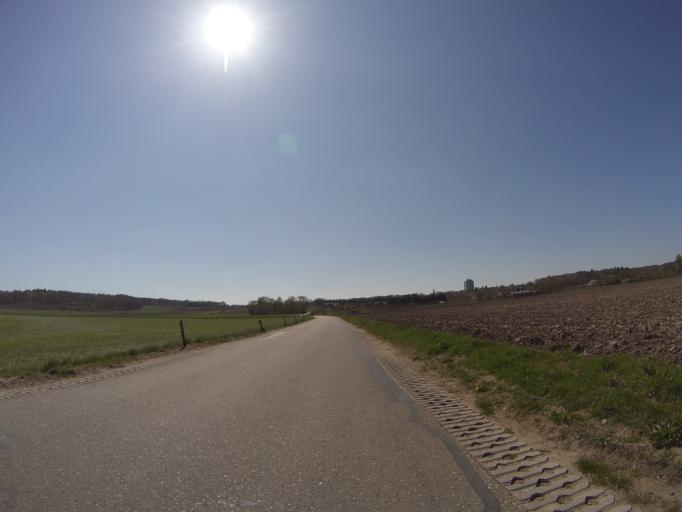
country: NL
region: Utrecht
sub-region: Gemeente Rhenen
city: Rhenen
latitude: 51.9691
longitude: 5.5881
